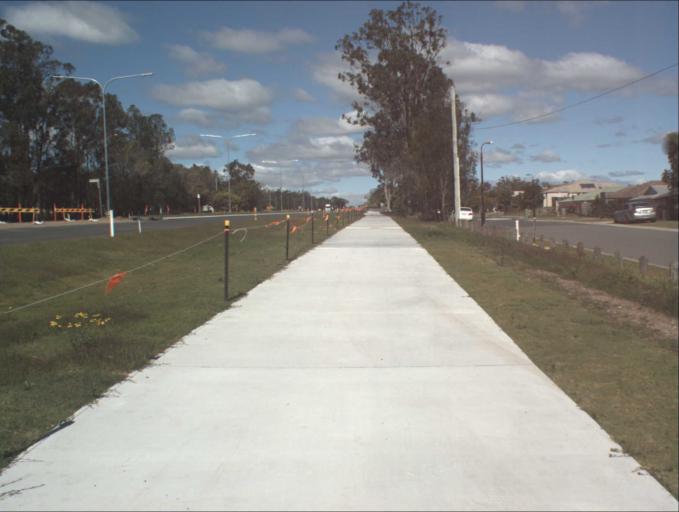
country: AU
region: Queensland
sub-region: Logan
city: Logan Reserve
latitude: -27.6965
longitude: 153.1016
